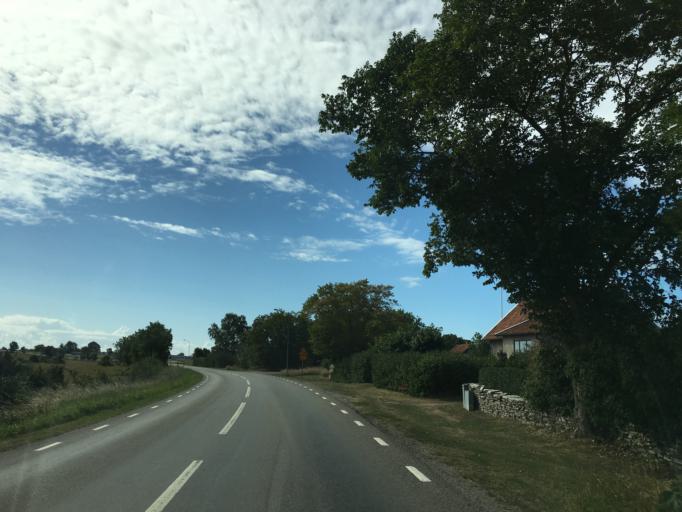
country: SE
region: Kalmar
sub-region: Morbylanga Kommun
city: Moerbylanga
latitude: 56.4452
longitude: 16.4266
